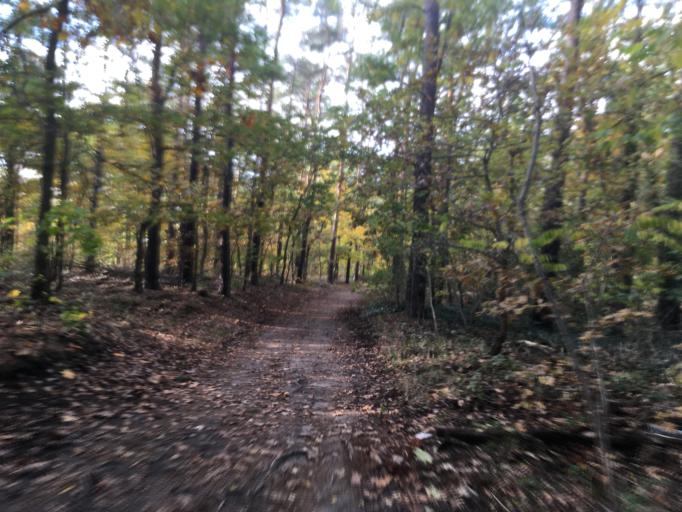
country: DE
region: Berlin
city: Kopenick Bezirk
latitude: 52.4665
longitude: 13.5602
